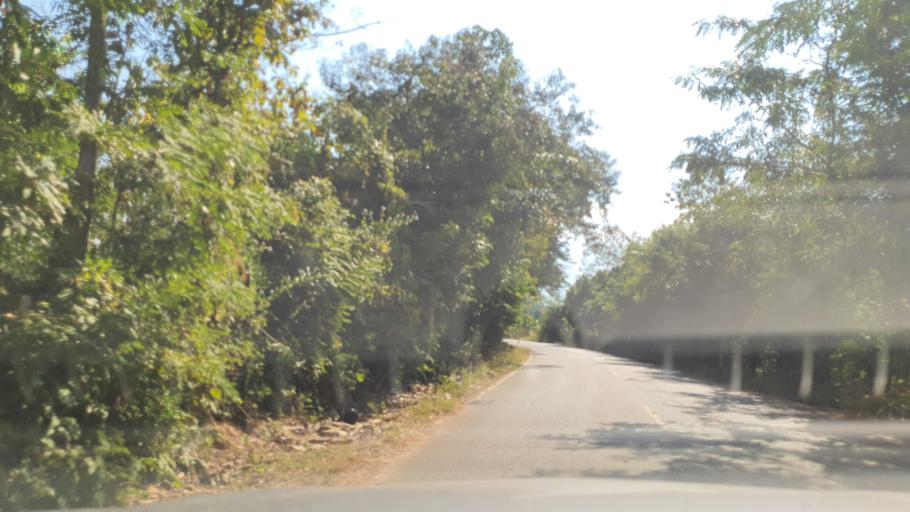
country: TH
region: Nan
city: Pua
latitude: 19.1461
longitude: 100.9193
